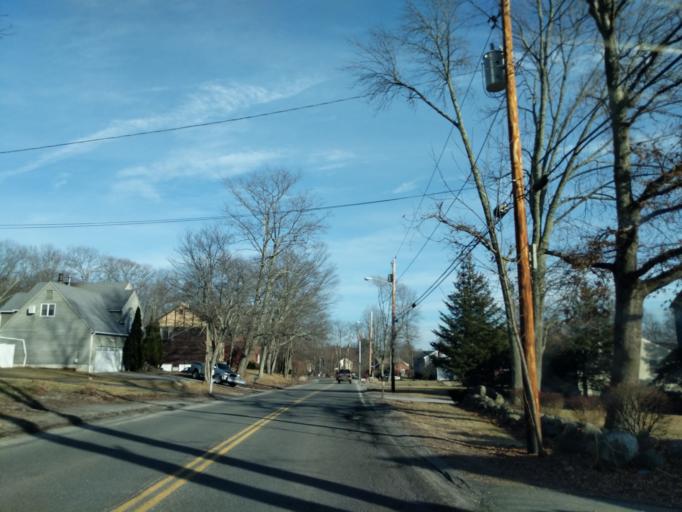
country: US
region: Massachusetts
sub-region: Worcester County
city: Blackstone
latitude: 42.0268
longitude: -71.5508
